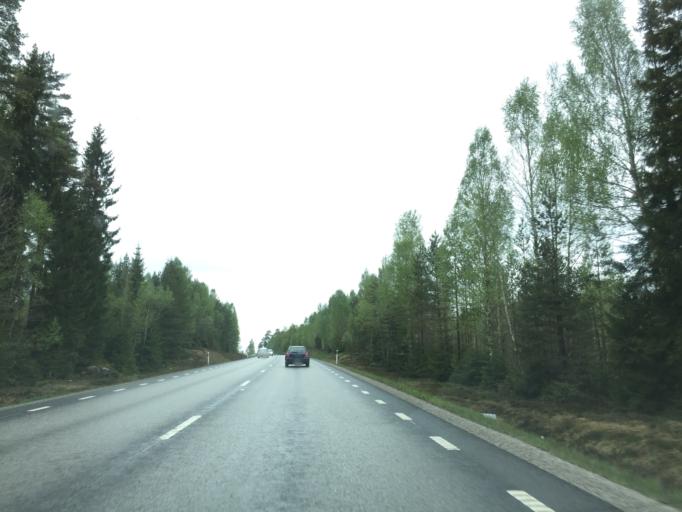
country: SE
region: OErebro
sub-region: Lindesbergs Kommun
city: Lindesberg
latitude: 59.5579
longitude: 15.2206
